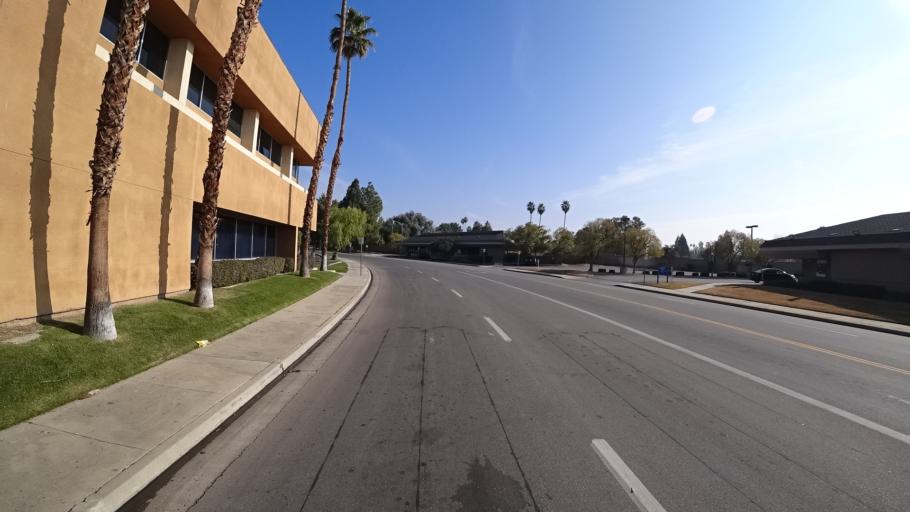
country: US
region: California
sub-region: Kern County
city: Bakersfield
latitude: 35.3923
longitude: -118.9495
